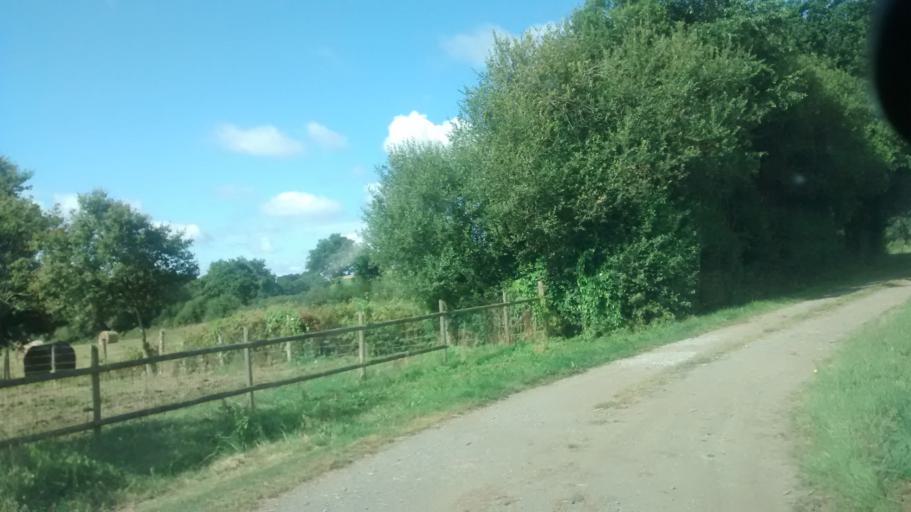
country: FR
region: Brittany
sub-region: Departement d'Ille-et-Vilaine
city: La Dominelais
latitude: 47.7752
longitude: -1.7197
